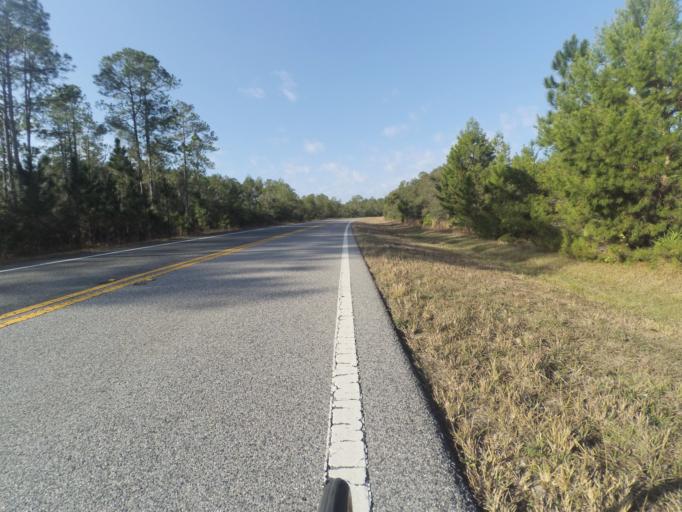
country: US
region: Florida
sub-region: Lake County
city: Astor
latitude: 29.1430
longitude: -81.5847
